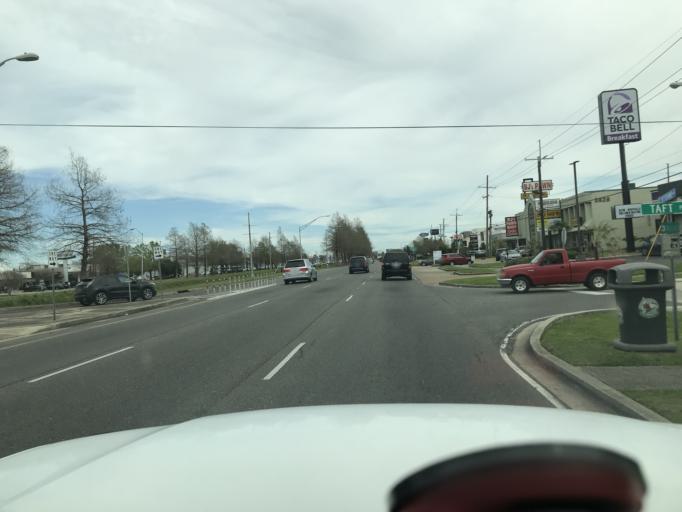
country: US
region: Louisiana
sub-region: Jefferson Parish
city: Metairie Terrace
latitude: 30.0041
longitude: -90.1705
